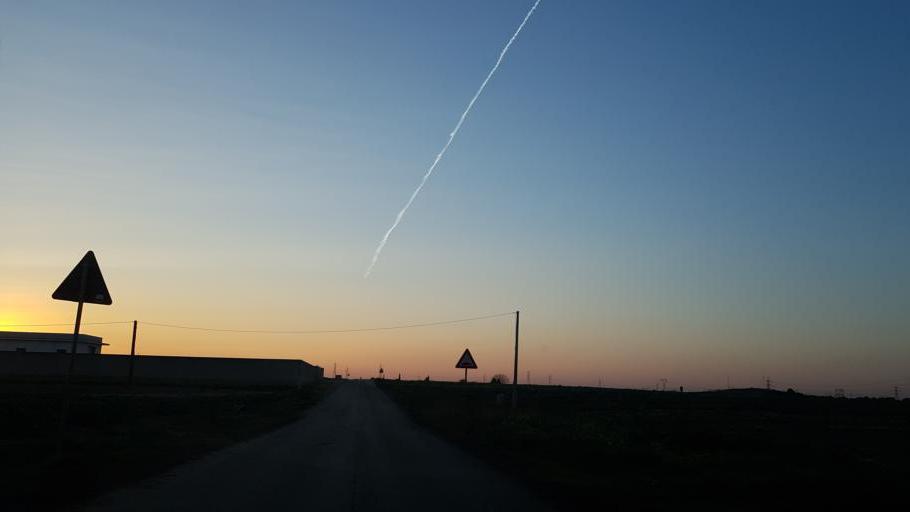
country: IT
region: Apulia
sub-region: Provincia di Brindisi
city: La Rosa
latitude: 40.5902
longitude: 17.9240
